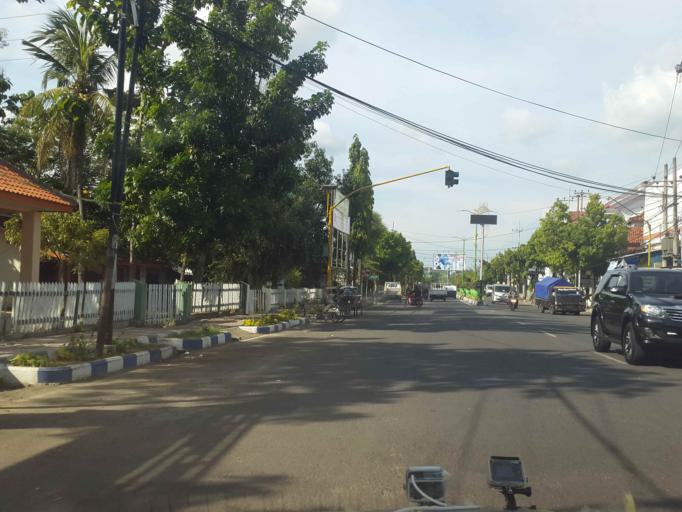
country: ID
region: East Java
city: Sumenep
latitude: -7.0186
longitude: 113.8576
